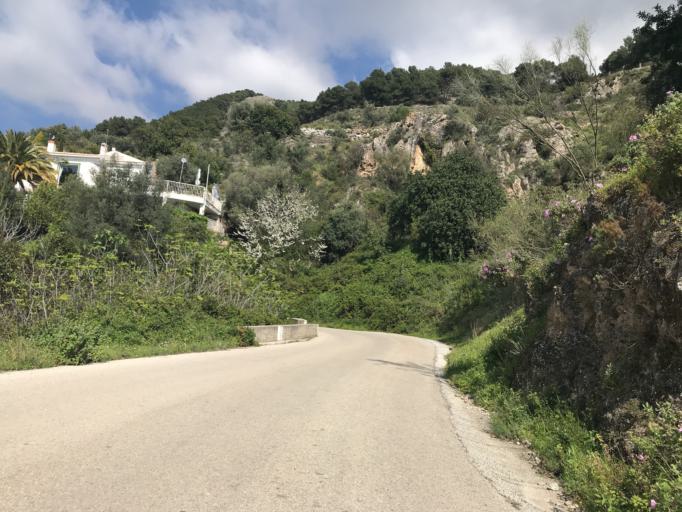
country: ES
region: Andalusia
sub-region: Provincia de Malaga
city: Alcaucin
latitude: 36.9071
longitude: -4.1109
